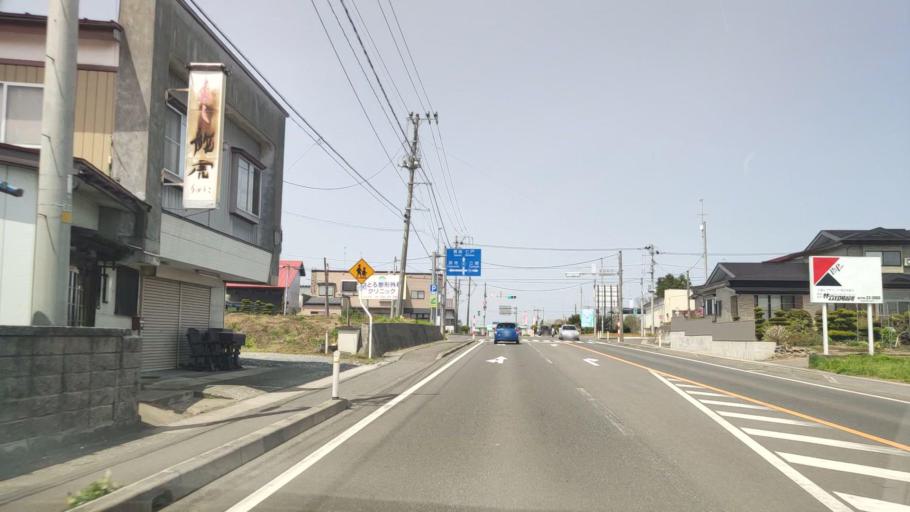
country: JP
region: Aomori
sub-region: Misawa Shi
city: Inuotose
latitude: 40.6578
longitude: 141.1923
